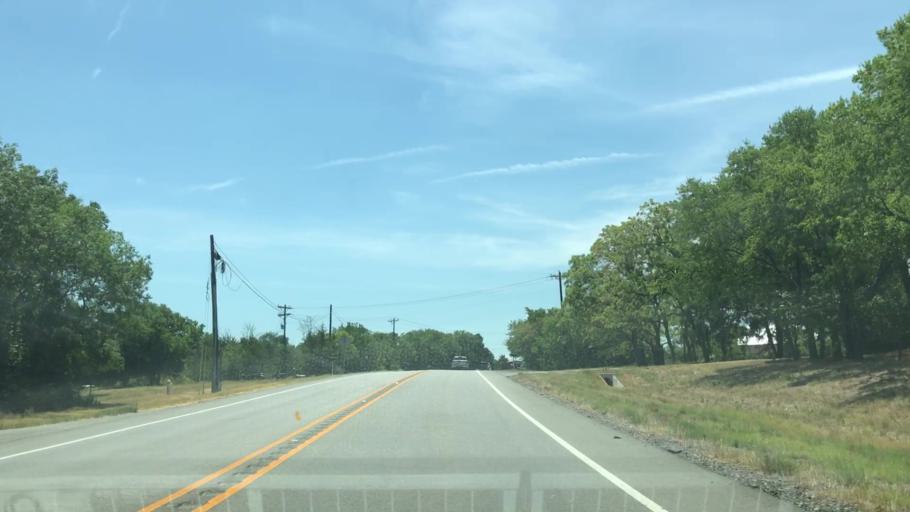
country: US
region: Texas
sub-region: Collin County
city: Lucas
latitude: 33.1170
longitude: -96.6035
